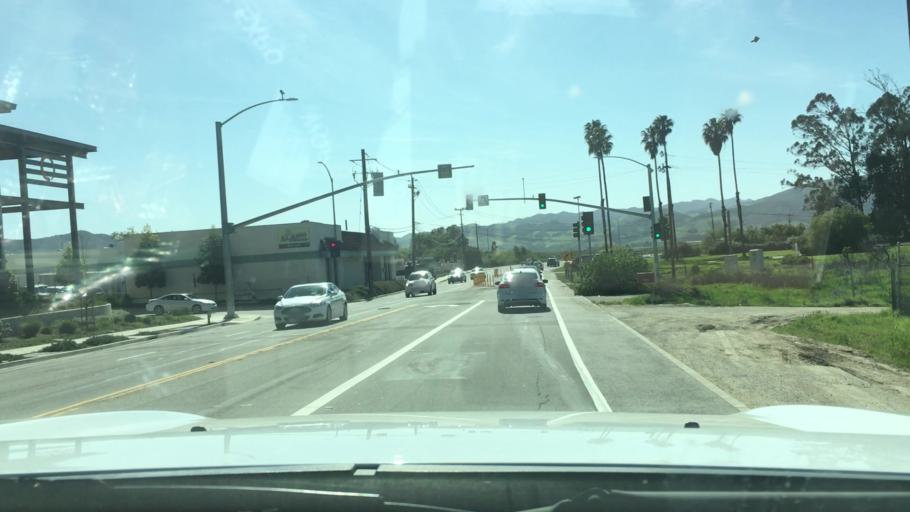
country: US
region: California
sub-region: San Luis Obispo County
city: San Luis Obispo
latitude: 35.2476
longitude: -120.6452
